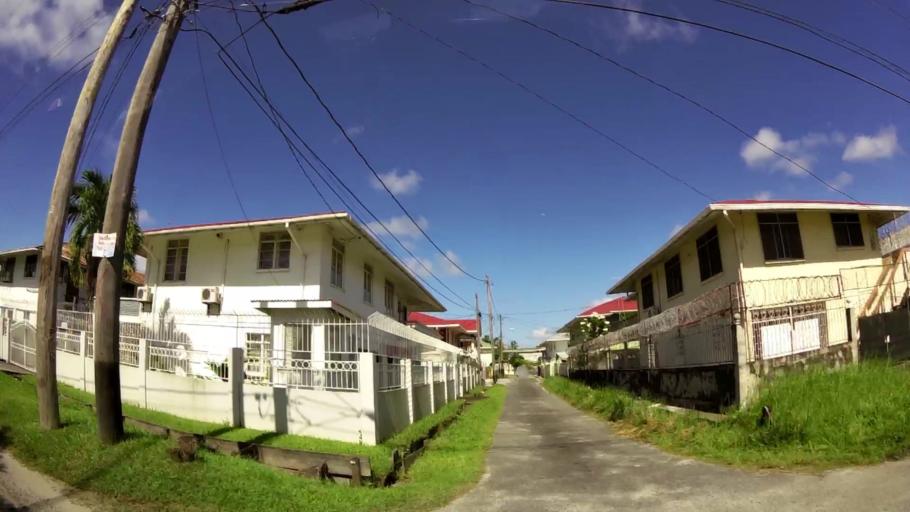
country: GY
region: Demerara-Mahaica
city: Georgetown
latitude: 6.8099
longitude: -58.1412
